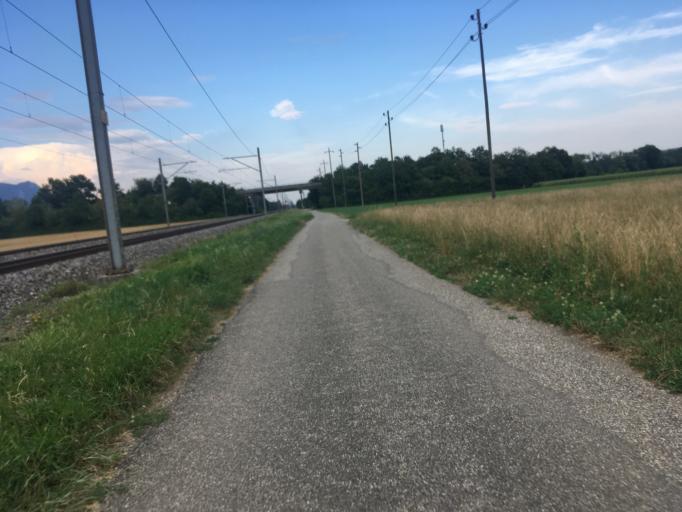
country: CH
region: Solothurn
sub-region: Bezirk Lebern
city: Bettlach
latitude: 47.1969
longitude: 7.4387
